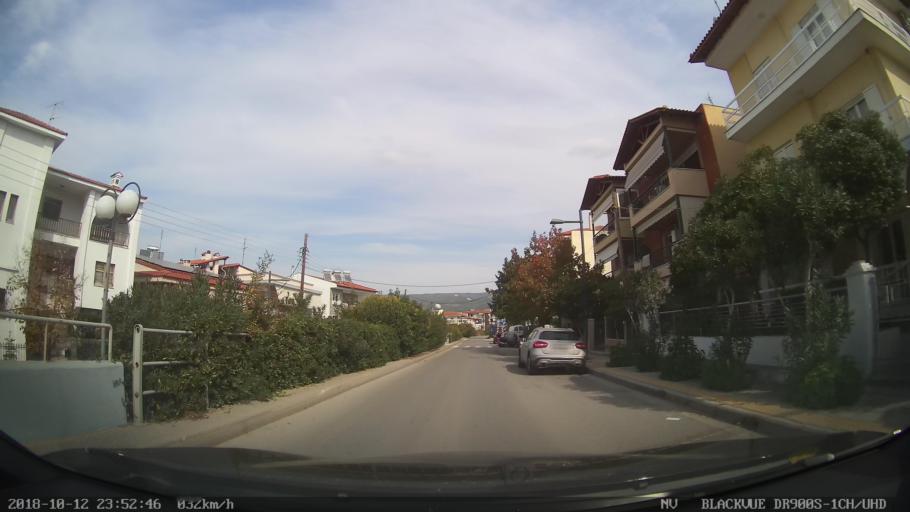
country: GR
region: Central Macedonia
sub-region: Nomos Thessalonikis
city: Pylaia
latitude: 40.5991
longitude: 22.9808
